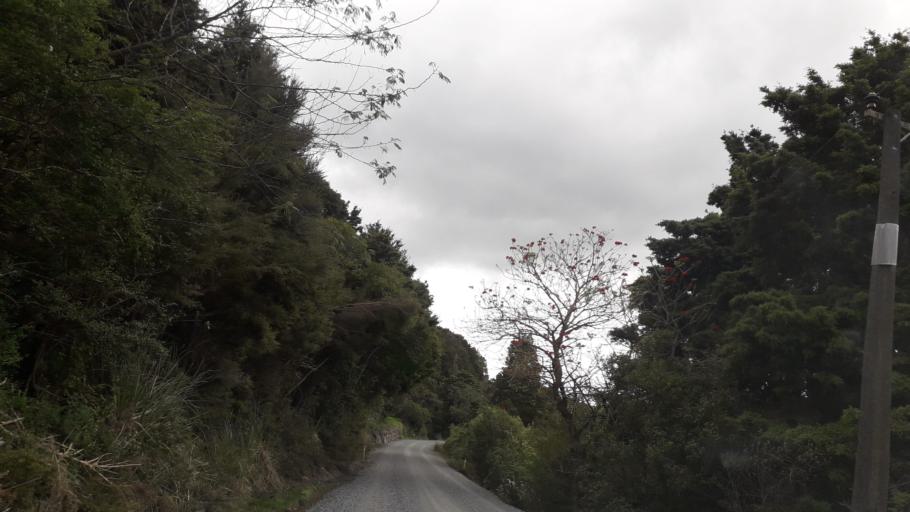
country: NZ
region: Northland
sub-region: Far North District
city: Kerikeri
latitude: -35.1319
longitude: 173.7338
